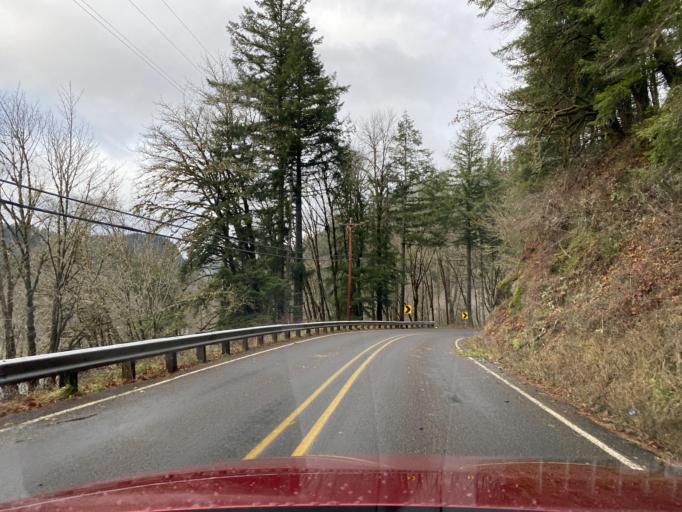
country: US
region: Oregon
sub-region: Lane County
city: Oakridge
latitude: 43.7567
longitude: -122.5255
